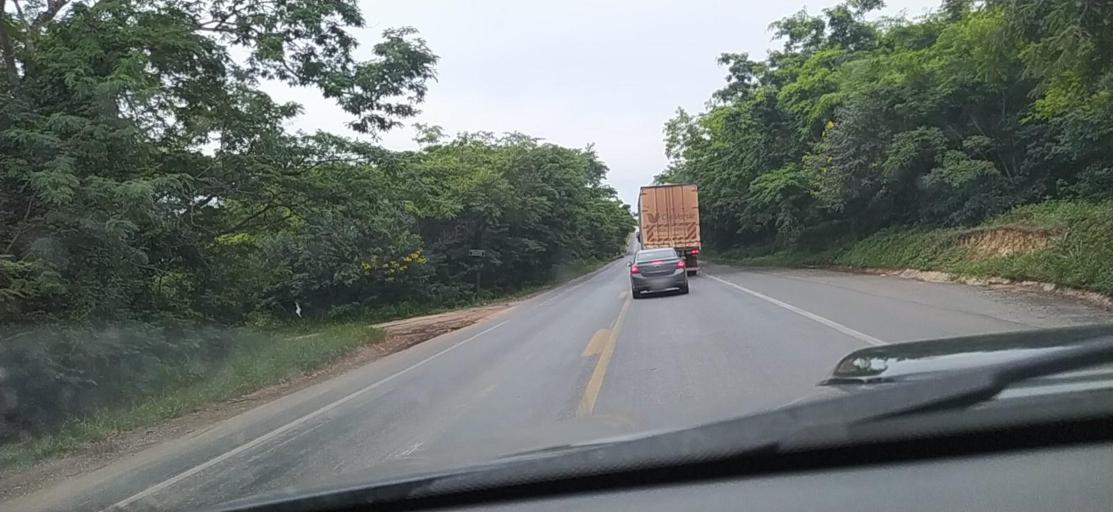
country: BR
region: Minas Gerais
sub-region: Montes Claros
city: Montes Claros
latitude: -16.6602
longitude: -43.7489
